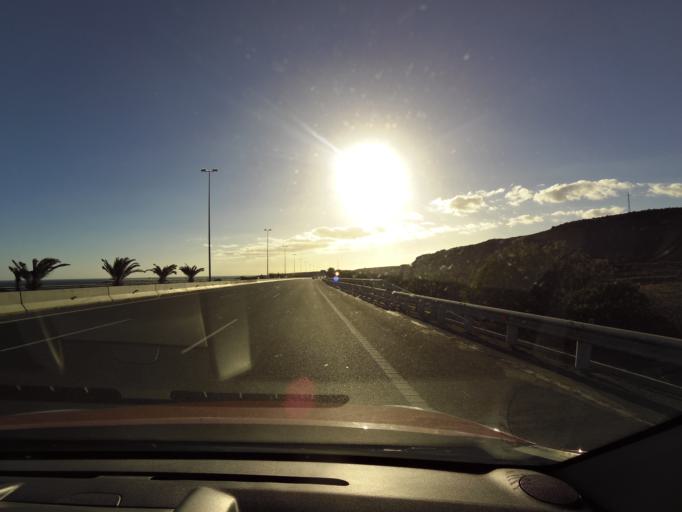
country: ES
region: Canary Islands
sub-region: Provincia de Las Palmas
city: Playa del Ingles
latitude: 27.7956
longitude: -15.4916
